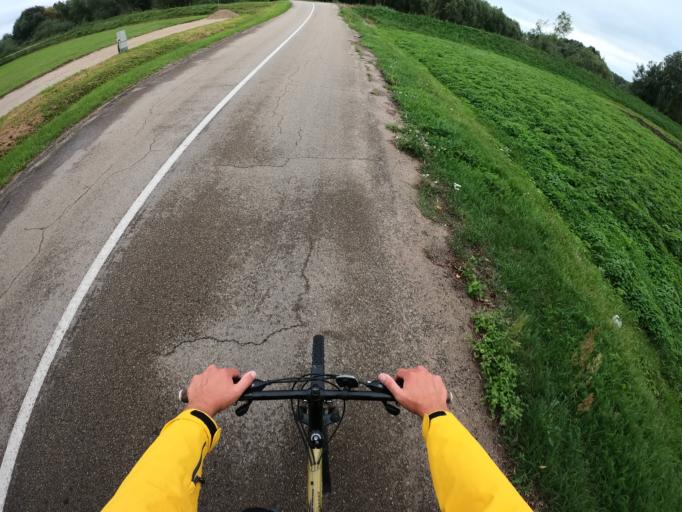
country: LT
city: Rusne
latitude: 55.3432
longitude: 21.3255
